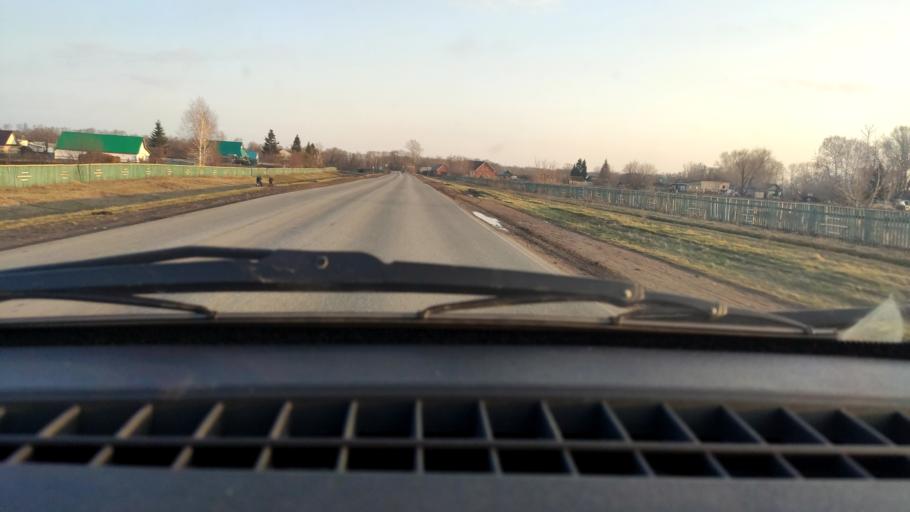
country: RU
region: Bashkortostan
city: Davlekanovo
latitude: 54.3702
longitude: 55.1951
